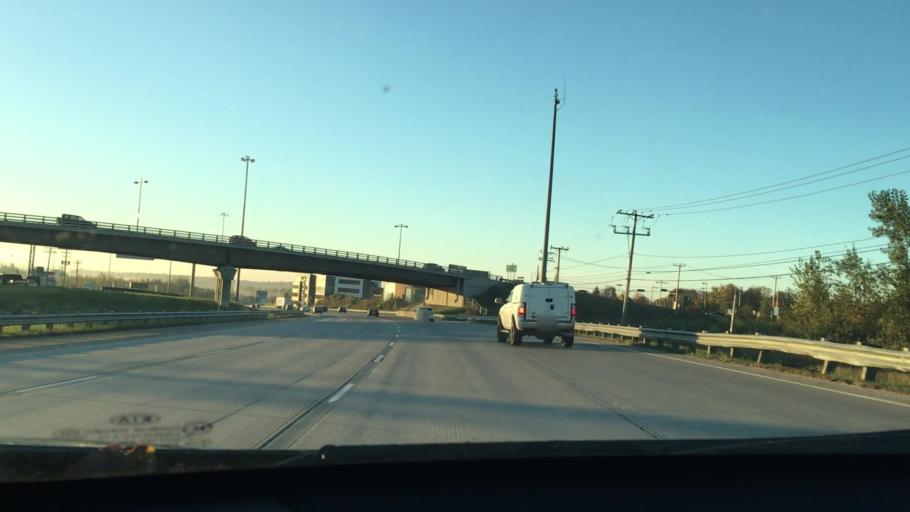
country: CA
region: Quebec
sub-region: Laurentides
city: Saint-Jerome
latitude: 45.7584
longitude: -74.0207
